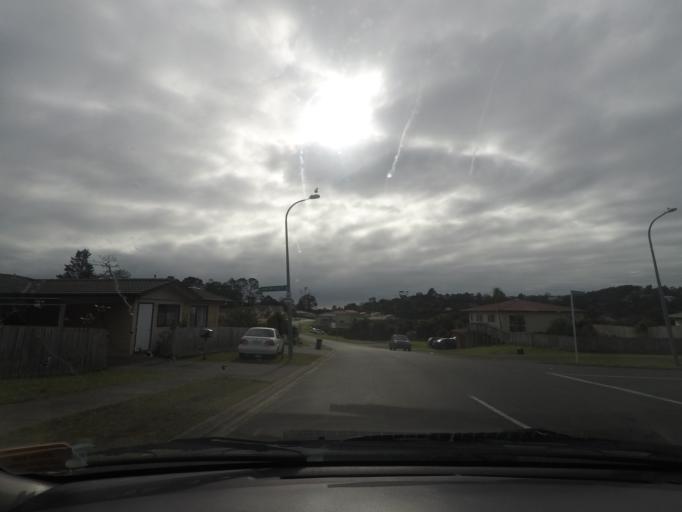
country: NZ
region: Auckland
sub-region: Auckland
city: Waitakere
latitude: -36.9062
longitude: 174.6331
